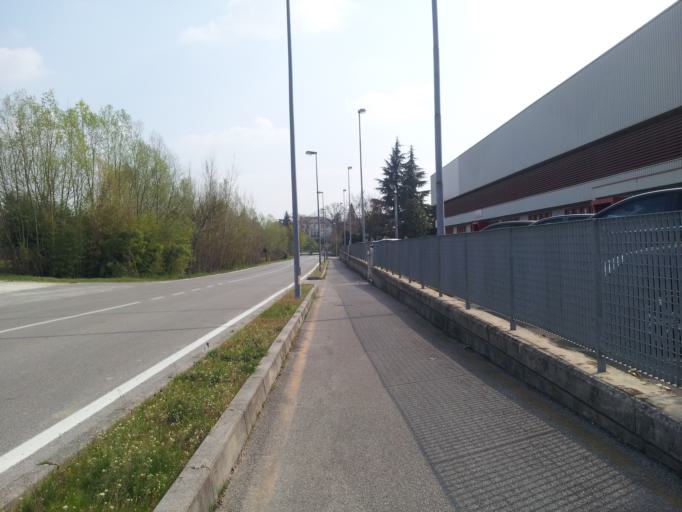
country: IT
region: Friuli Venezia Giulia
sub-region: Provincia di Pordenone
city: Pasiano
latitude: 45.8547
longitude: 12.6266
